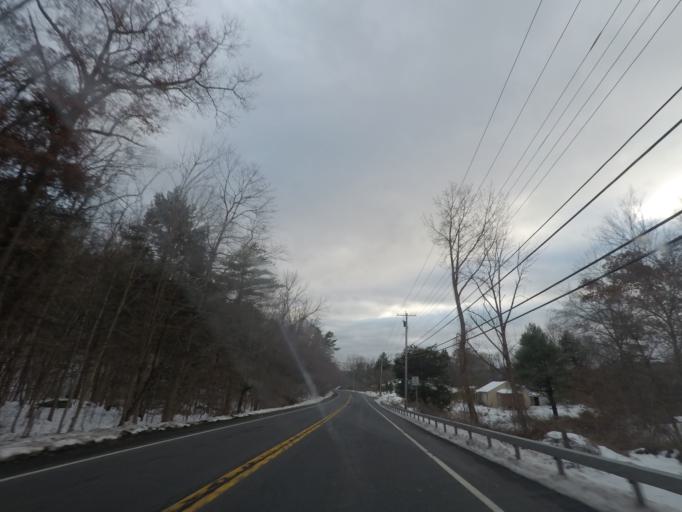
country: US
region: New York
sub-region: Ulster County
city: Hurley
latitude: 41.8928
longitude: -74.0392
